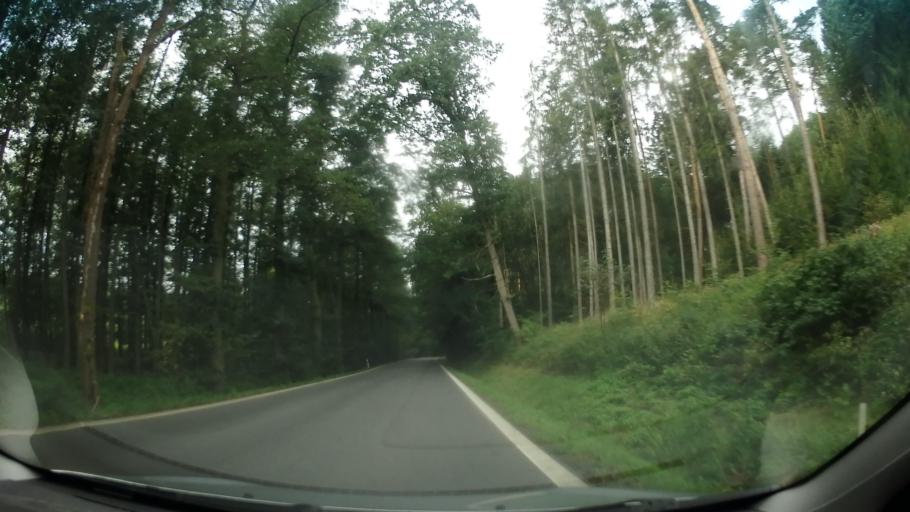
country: CZ
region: Central Bohemia
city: Bystrice
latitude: 49.7597
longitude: 14.6383
